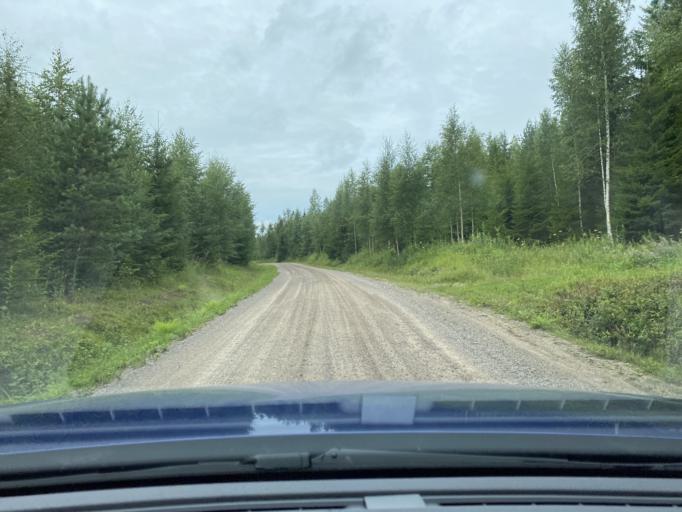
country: FI
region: Pirkanmaa
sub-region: Ylae-Pirkanmaa
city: Maenttae
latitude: 62.0179
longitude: 24.7484
